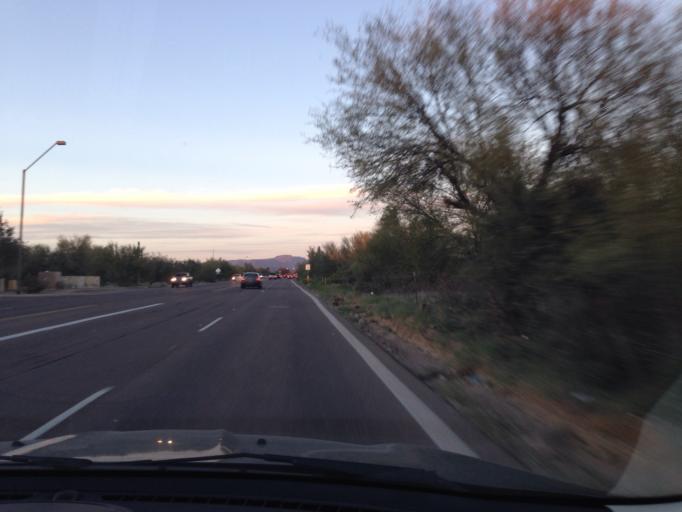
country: US
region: Arizona
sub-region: Maricopa County
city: Cave Creek
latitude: 33.7370
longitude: -111.9781
